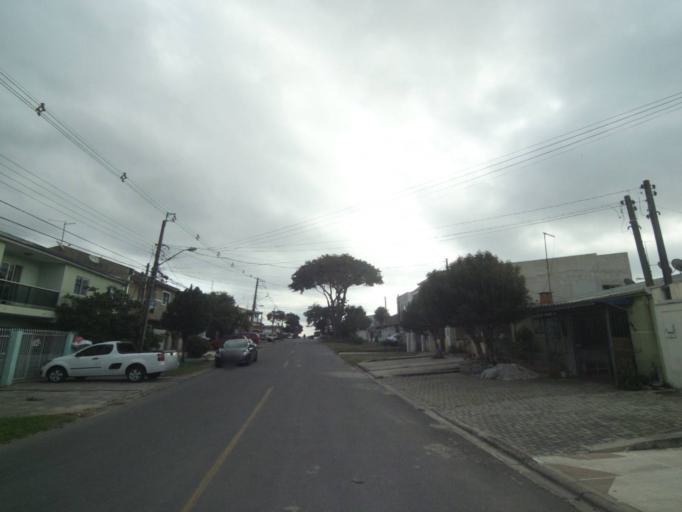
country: BR
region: Parana
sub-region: Sao Jose Dos Pinhais
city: Sao Jose dos Pinhais
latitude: -25.5429
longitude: -49.2476
